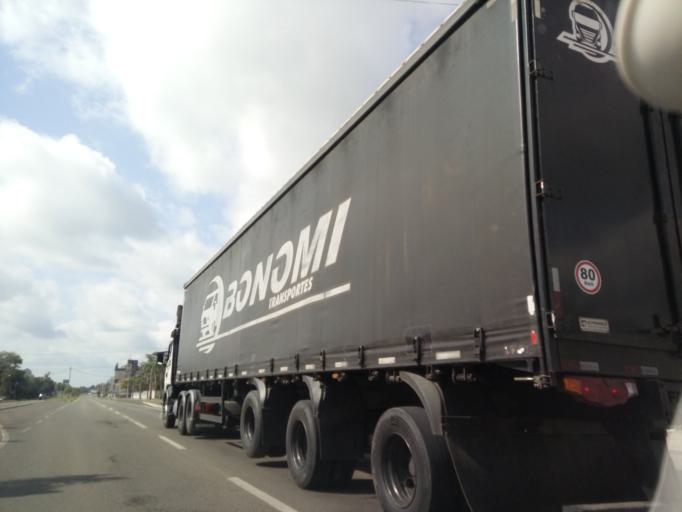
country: BR
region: Rio Grande do Sul
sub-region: Santa Maria
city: Santa Maria
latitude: -29.7027
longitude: -53.7143
